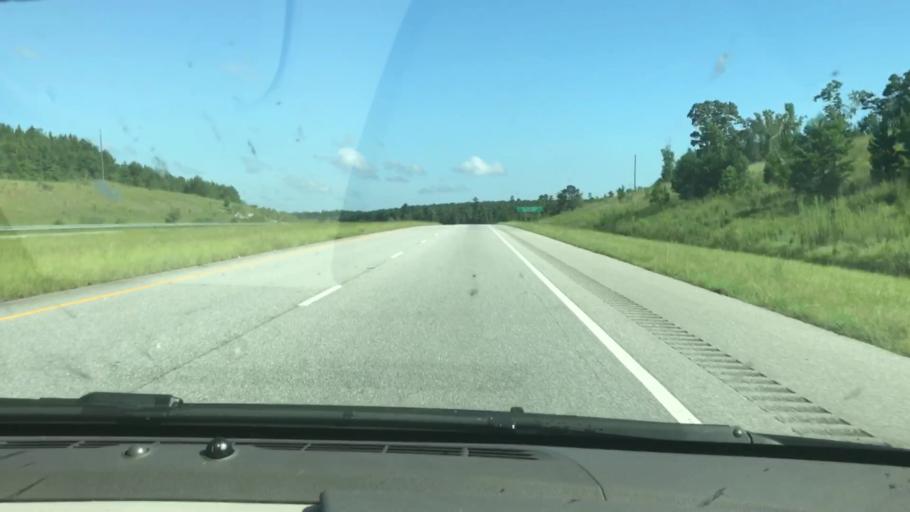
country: US
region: Alabama
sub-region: Barbour County
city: Eufaula
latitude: 32.1115
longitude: -85.1498
